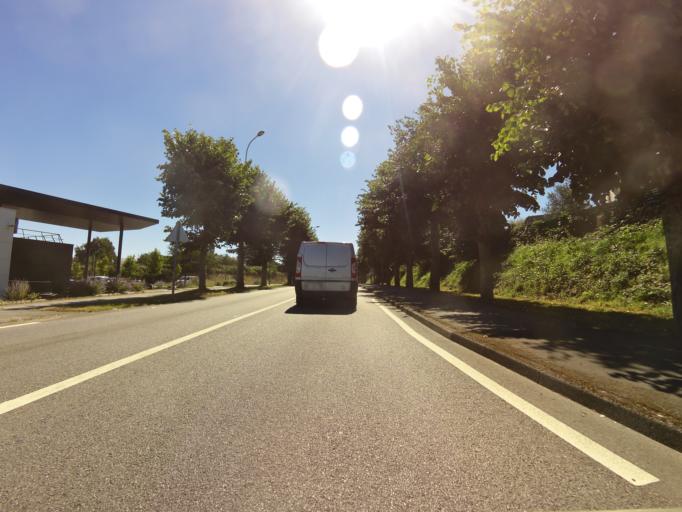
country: FR
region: Brittany
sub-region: Departement du Morbihan
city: Lanester
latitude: 47.7741
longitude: -3.3373
